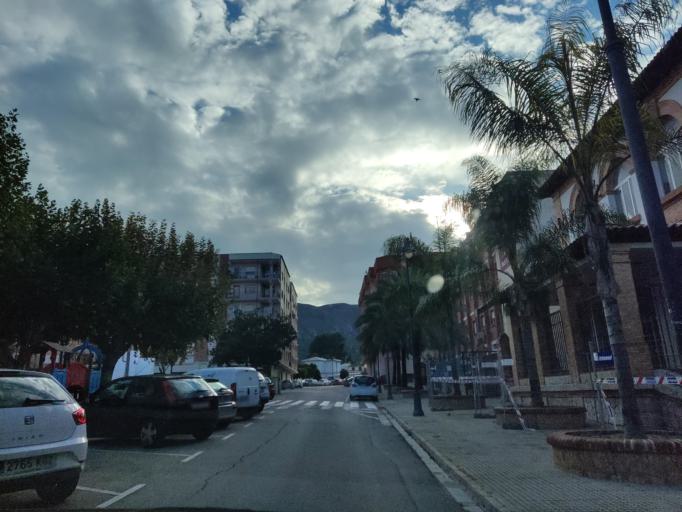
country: ES
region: Valencia
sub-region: Provincia de Alicante
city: Pego
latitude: 38.8395
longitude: -0.1206
